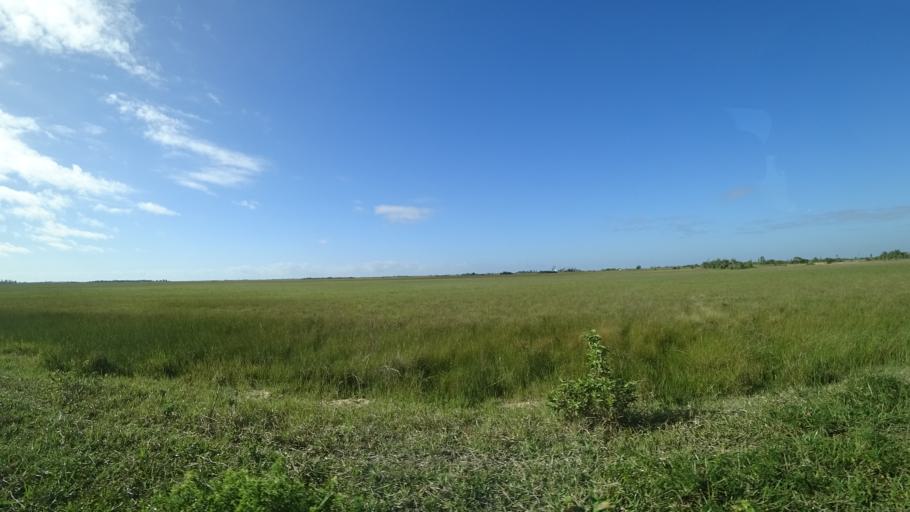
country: MZ
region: Sofala
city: Beira
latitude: -19.7305
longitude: 34.9810
